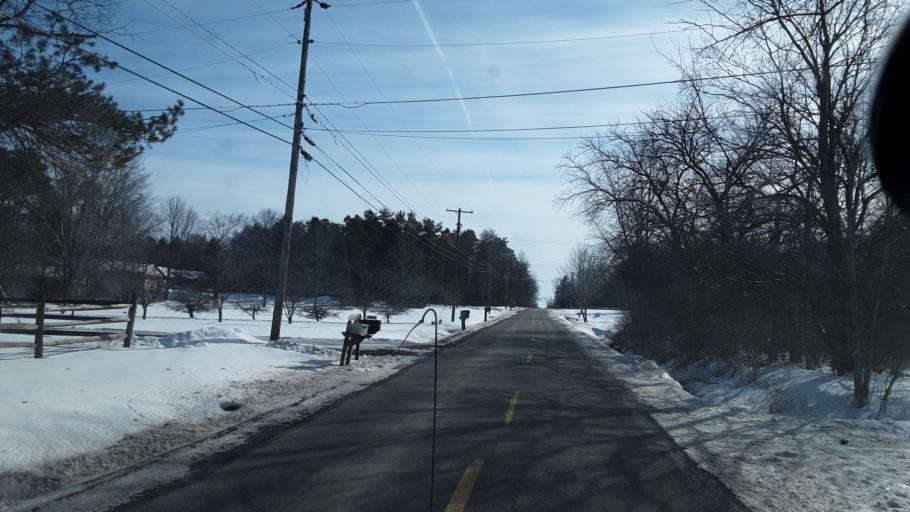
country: US
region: Ohio
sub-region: Columbiana County
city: Columbiana
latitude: 40.9499
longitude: -80.6978
